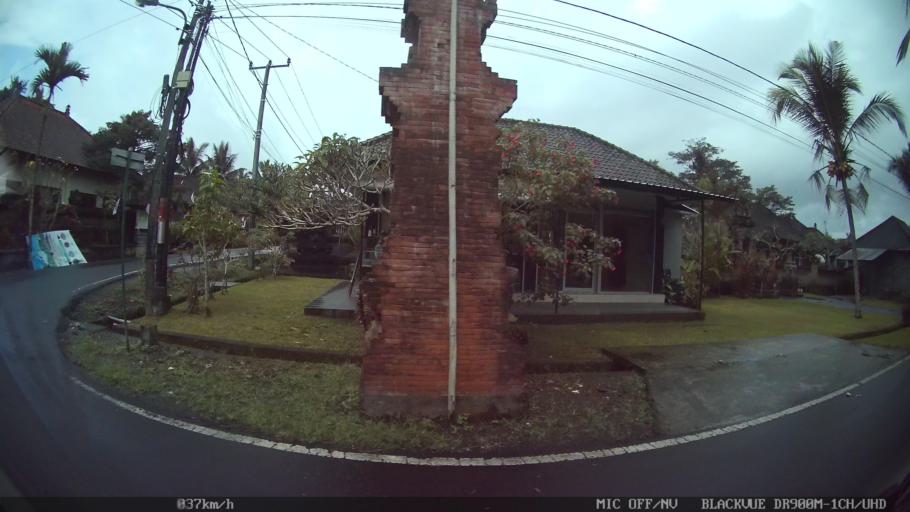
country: ID
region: Bali
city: Pegongan
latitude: -8.4887
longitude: 115.2384
